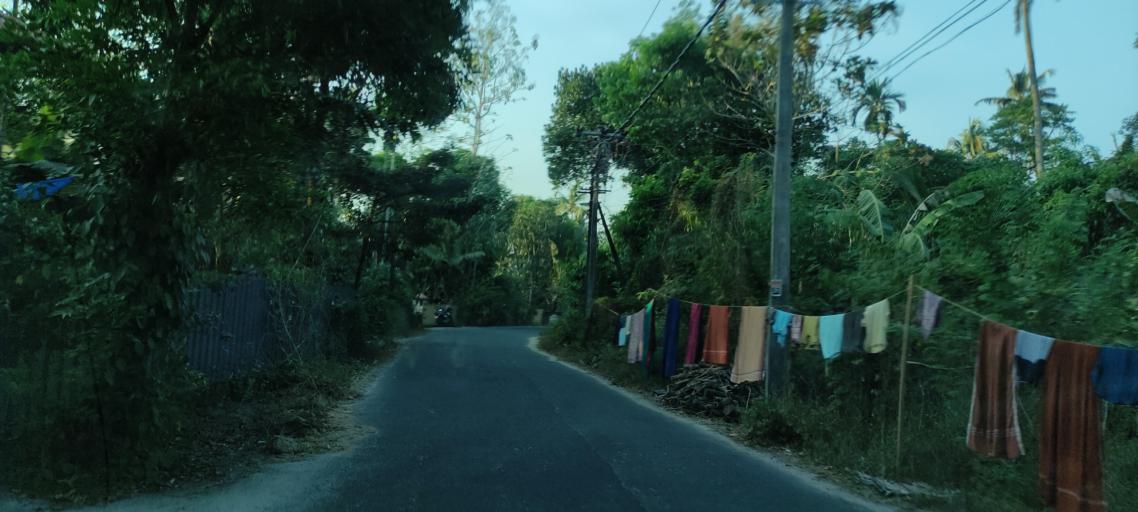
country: IN
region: Kerala
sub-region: Kottayam
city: Vaikam
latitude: 9.7594
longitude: 76.3536
